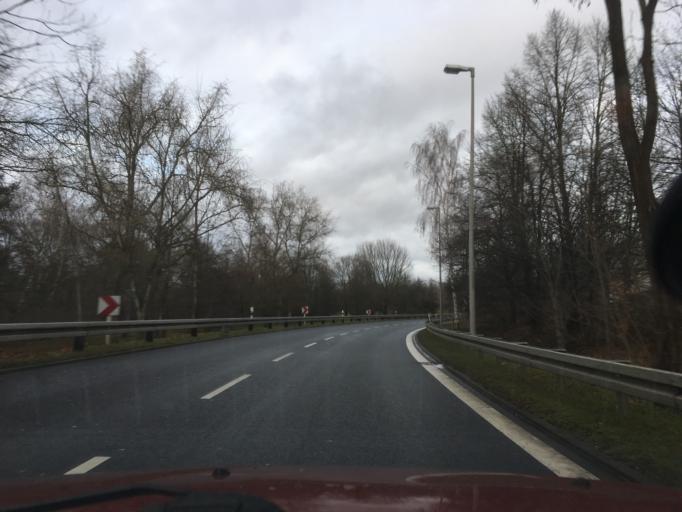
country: DE
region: Berlin
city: Bohnsdorf
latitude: 52.4024
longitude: 13.5548
